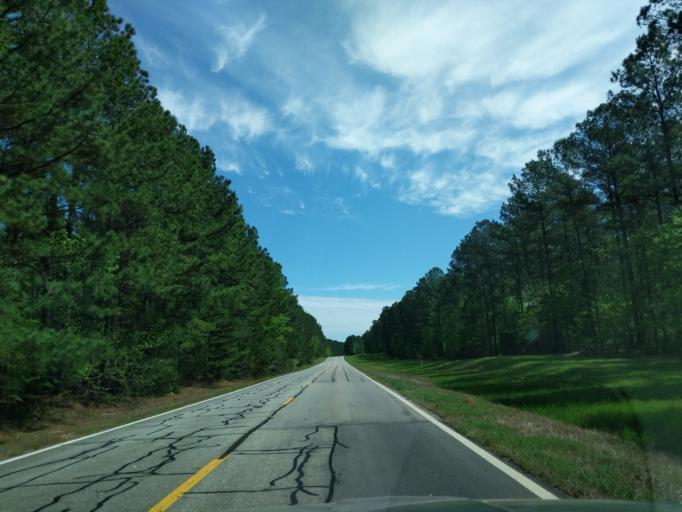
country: US
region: Georgia
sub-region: Columbia County
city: Appling
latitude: 33.6161
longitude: -82.2957
